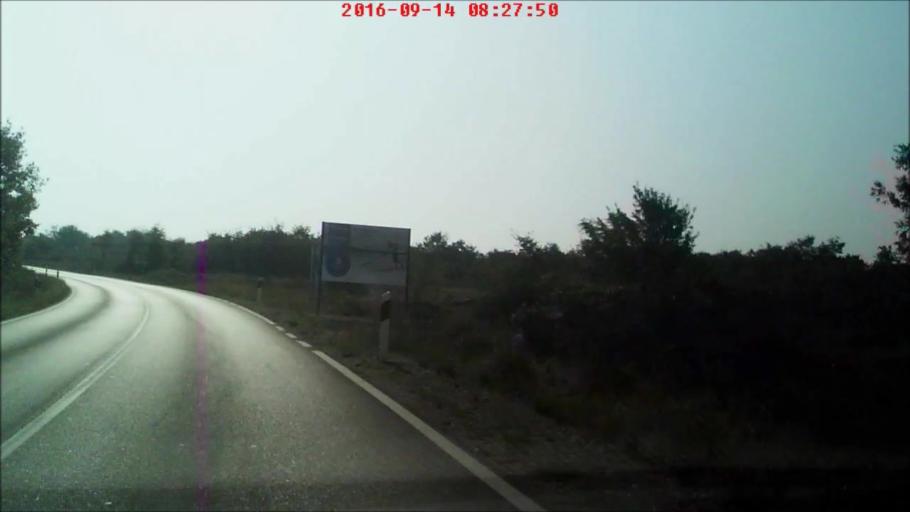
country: HR
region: Zadarska
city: Zadar
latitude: 44.1867
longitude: 15.2703
